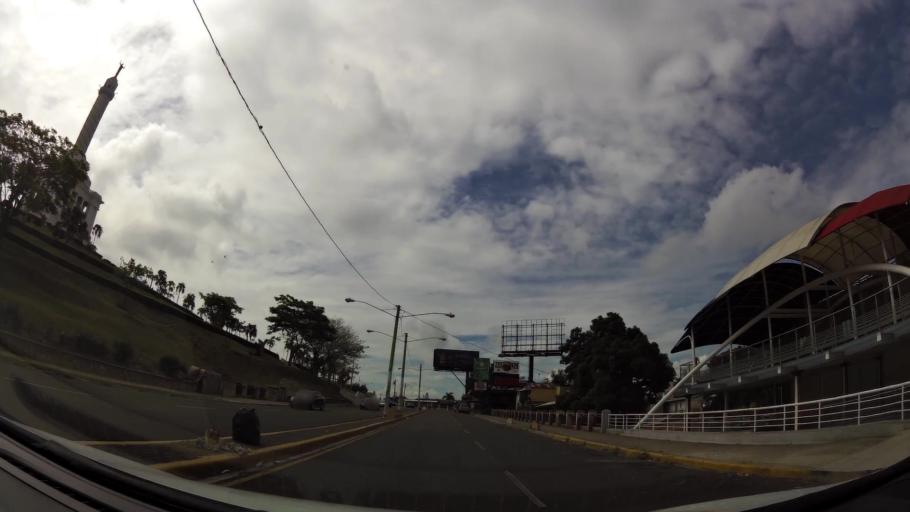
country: DO
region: Santiago
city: Santiago de los Caballeros
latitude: 19.4518
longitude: -70.6956
